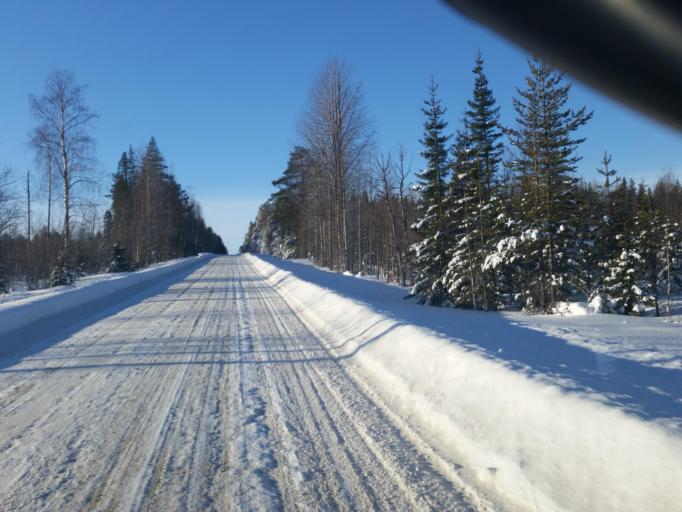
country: SE
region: Norrbotten
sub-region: Pitea Kommun
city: Roknas
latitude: 65.2142
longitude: 21.2364
